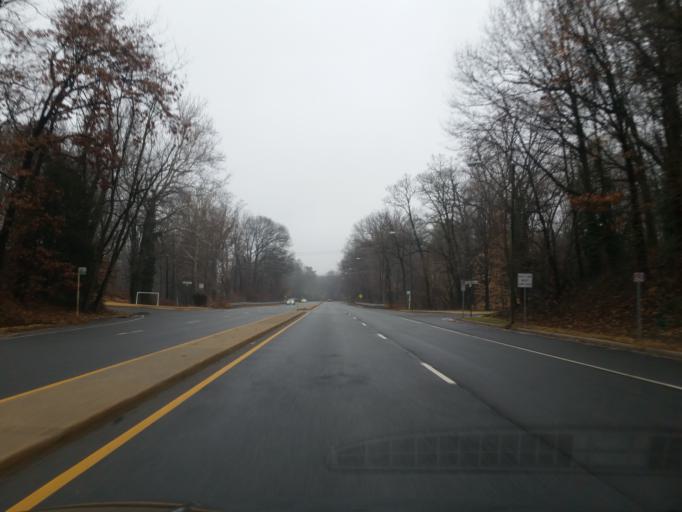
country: US
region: Maryland
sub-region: Montgomery County
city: Brookmont
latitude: 38.9225
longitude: -77.1286
